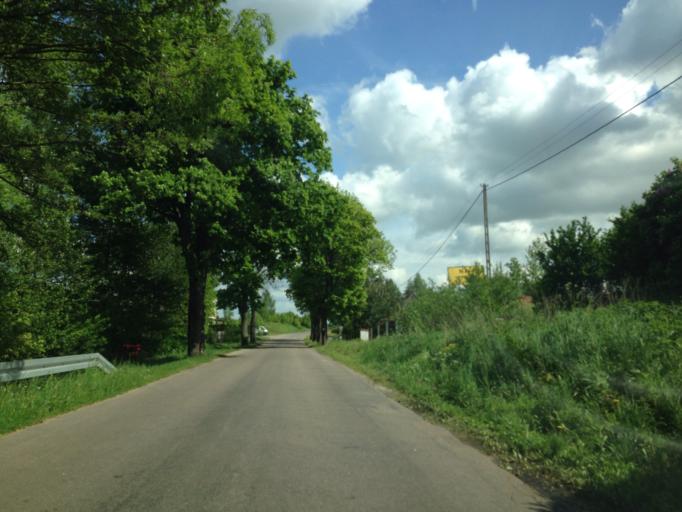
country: PL
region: Warmian-Masurian Voivodeship
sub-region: Powiat nidzicki
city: Kozlowo
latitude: 53.4152
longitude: 20.2621
